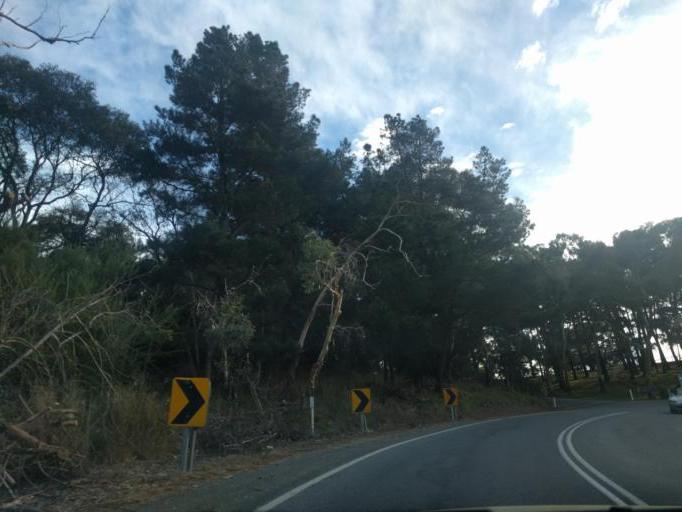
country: AU
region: South Australia
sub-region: Mount Barker
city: Little Hampton
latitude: -35.0482
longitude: 138.8357
